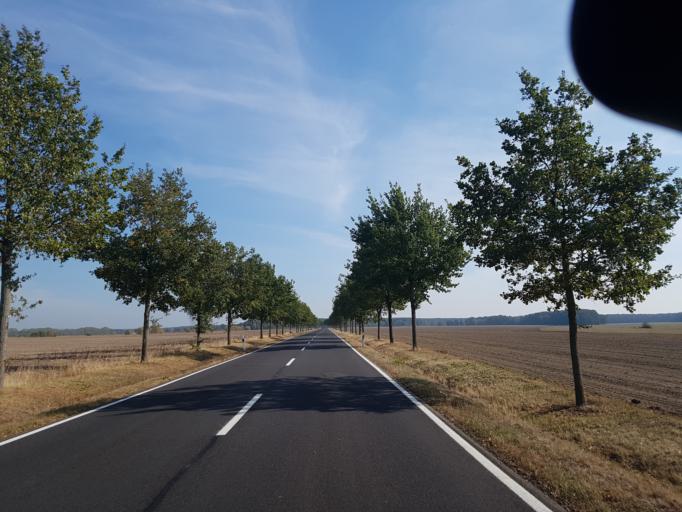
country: DE
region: Brandenburg
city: Ihlow
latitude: 51.8252
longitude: 13.3598
